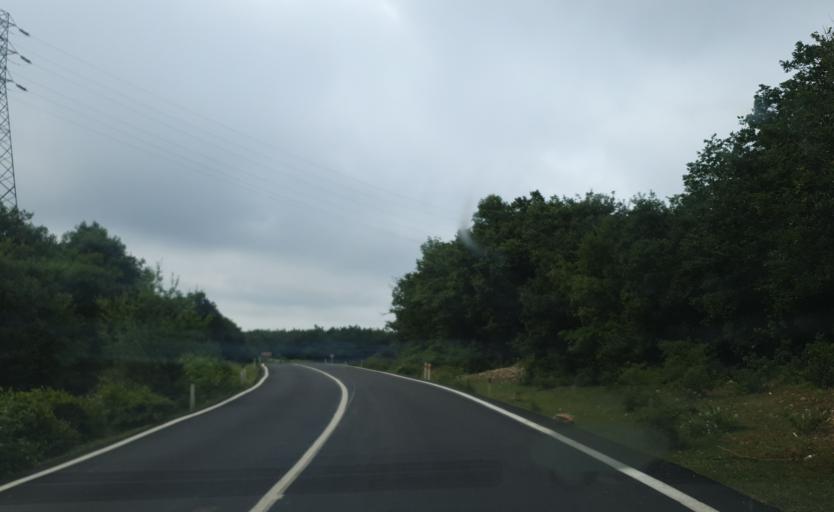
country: TR
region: Kirklareli
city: Salmydessus
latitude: 41.5976
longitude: 28.0833
